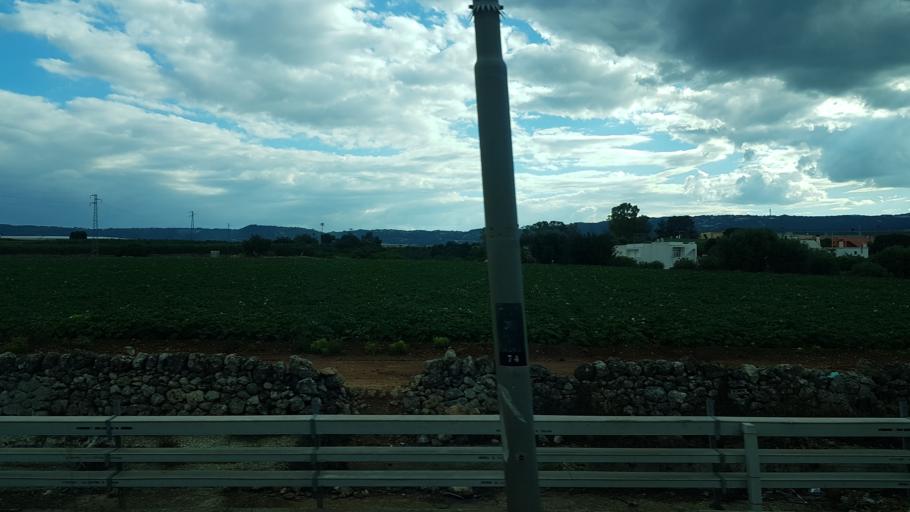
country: IT
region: Apulia
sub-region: Provincia di Brindisi
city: Fasano
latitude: 40.8492
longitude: 17.3894
